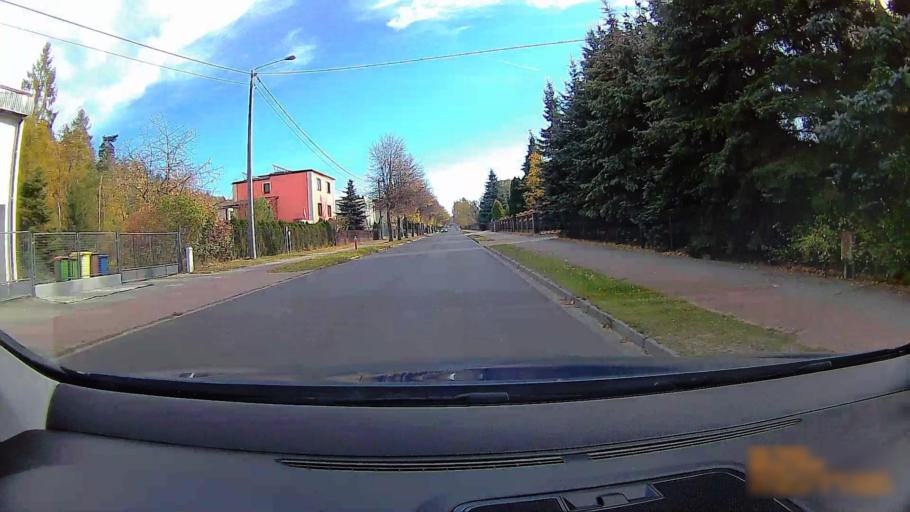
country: PL
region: Greater Poland Voivodeship
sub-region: Powiat ostrzeszowski
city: Ostrzeszow
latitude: 51.4338
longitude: 17.9242
